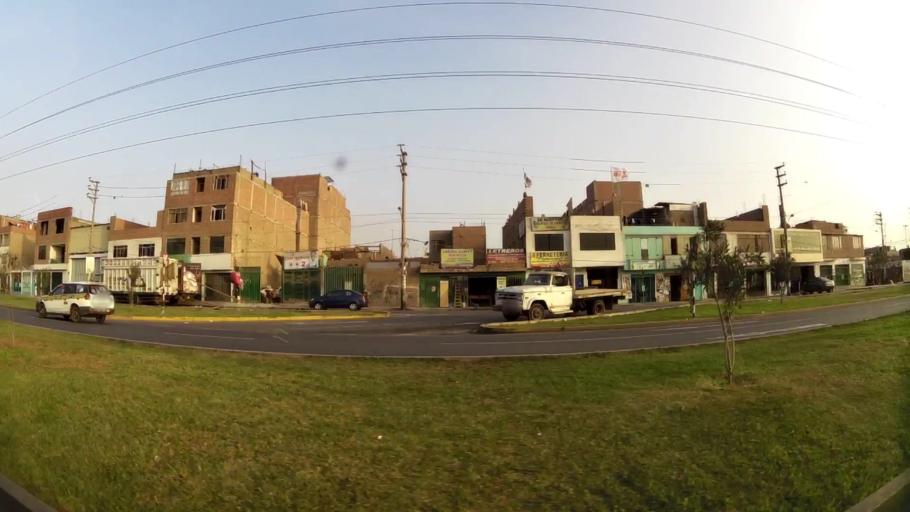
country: PE
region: Lima
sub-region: Lima
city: Independencia
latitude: -11.9899
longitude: -77.1003
